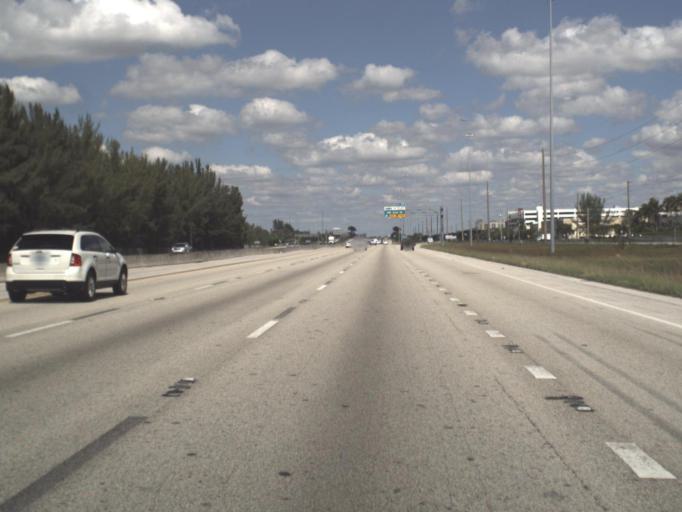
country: US
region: Florida
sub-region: Miami-Dade County
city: Doral
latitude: 25.8014
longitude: -80.3859
